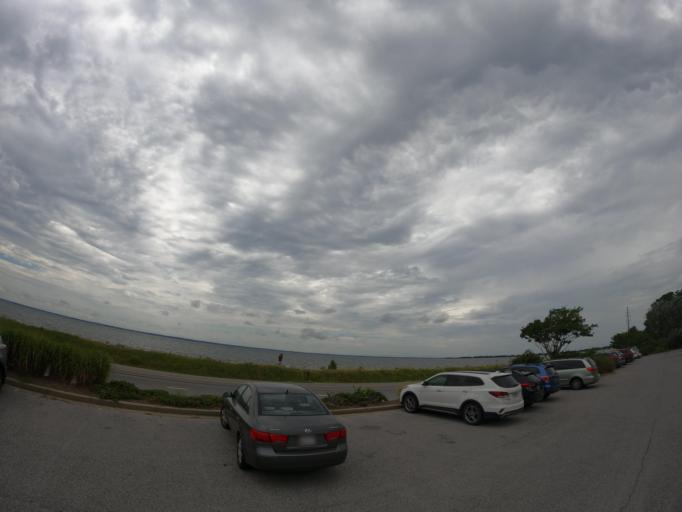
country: US
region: Maryland
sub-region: Saint Mary's County
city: Lexington Park
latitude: 38.1305
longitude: -76.4949
